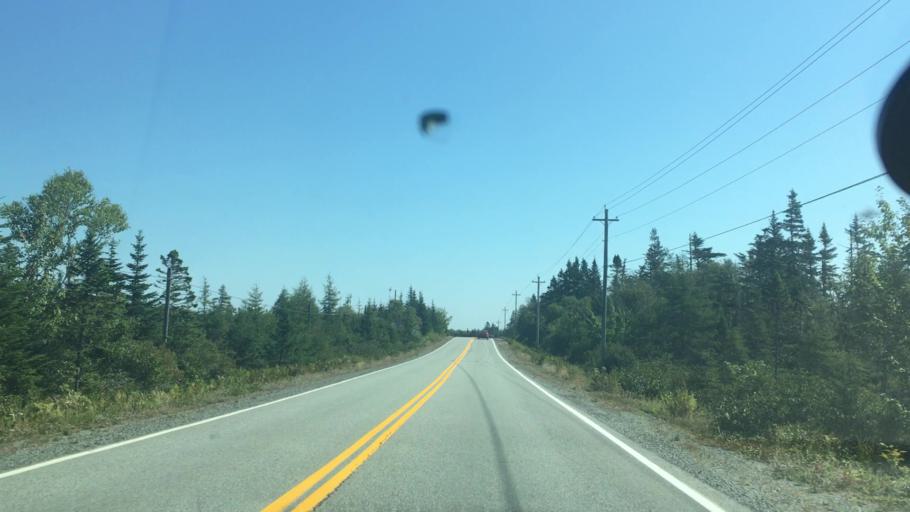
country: CA
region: Nova Scotia
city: Antigonish
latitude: 44.9341
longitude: -62.2787
